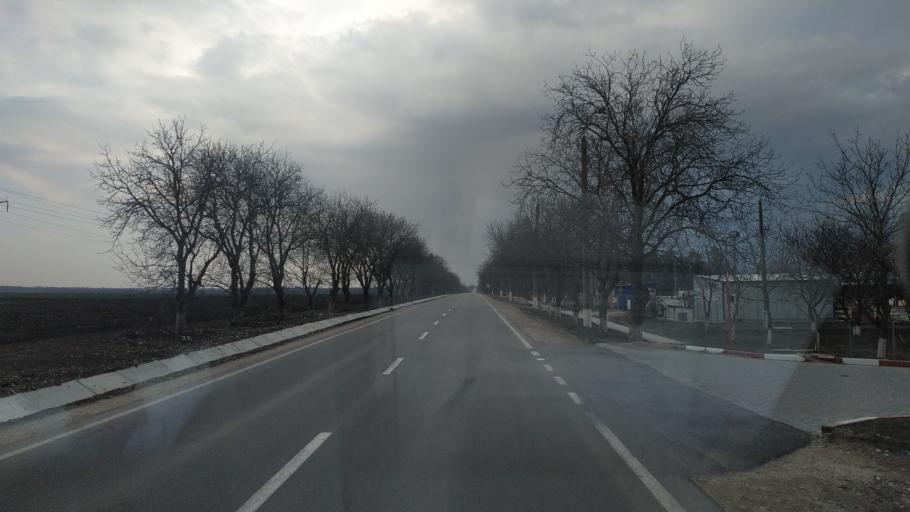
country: MD
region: Telenesti
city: Grigoriopol
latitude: 47.0164
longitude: 29.2894
